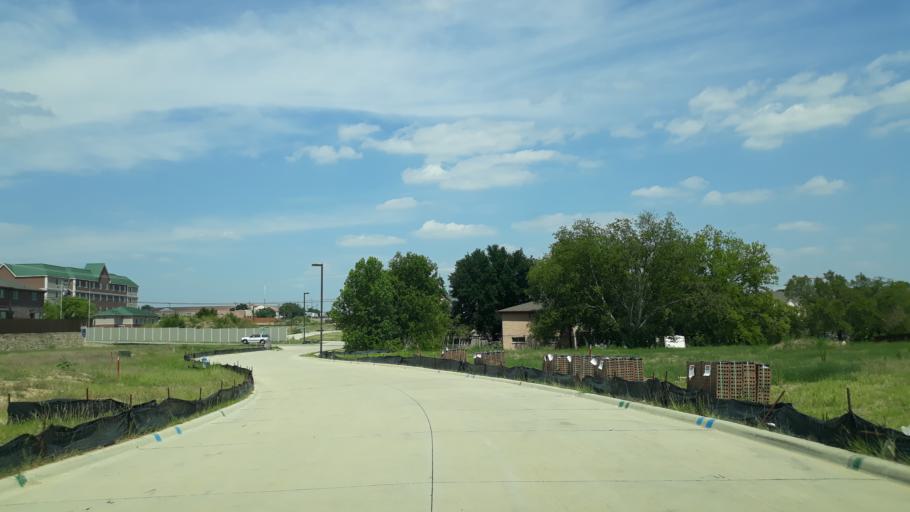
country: US
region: Texas
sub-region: Tarrant County
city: Euless
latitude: 32.8338
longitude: -97.0145
